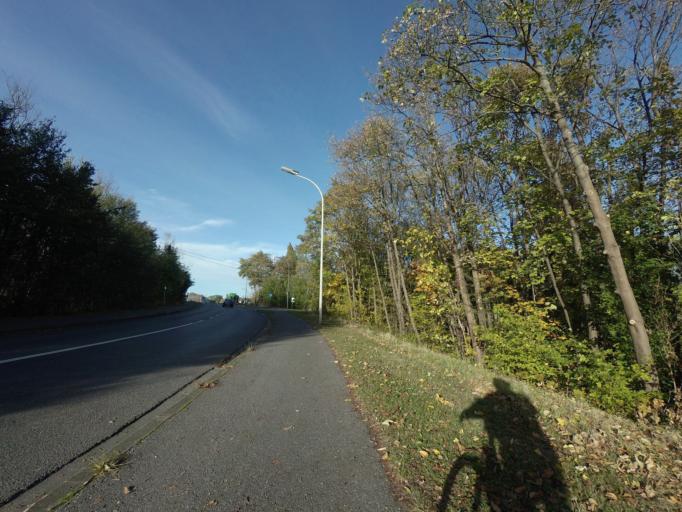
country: BE
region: Flanders
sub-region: Provincie Antwerpen
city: Kapellen
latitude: 51.2660
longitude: 4.4487
